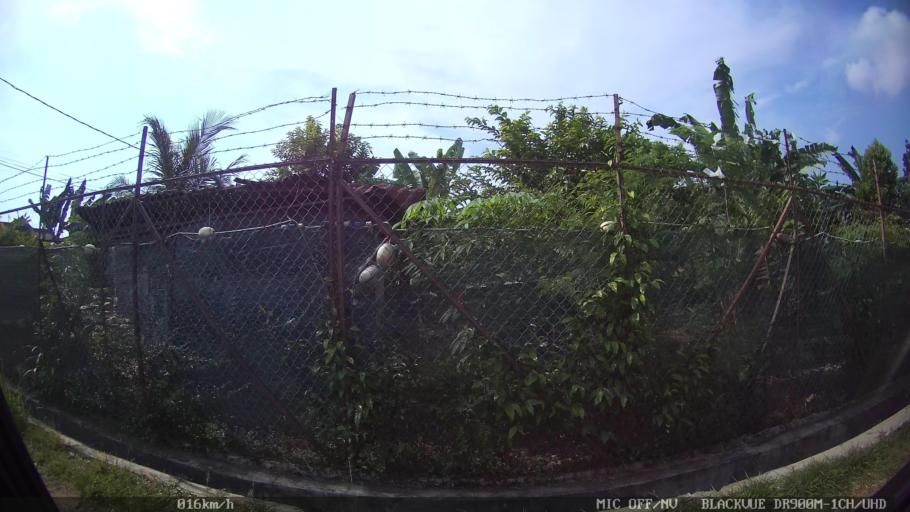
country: ID
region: Lampung
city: Kedaton
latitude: -5.3857
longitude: 105.2343
